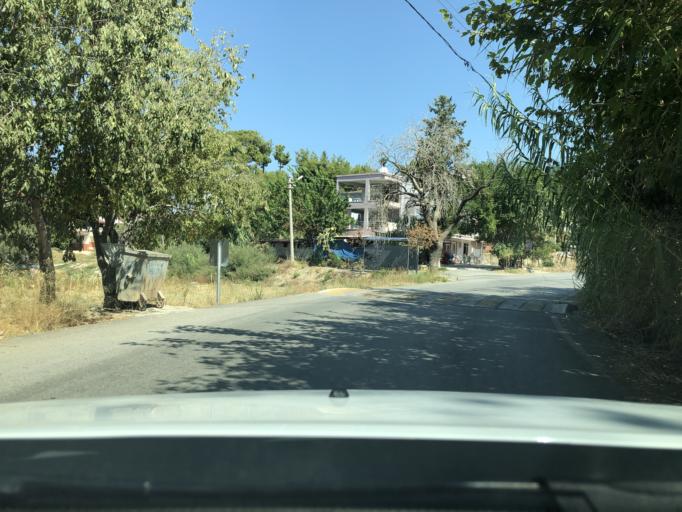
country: TR
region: Antalya
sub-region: Manavgat
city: Manavgat
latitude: 36.8134
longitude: 31.4885
